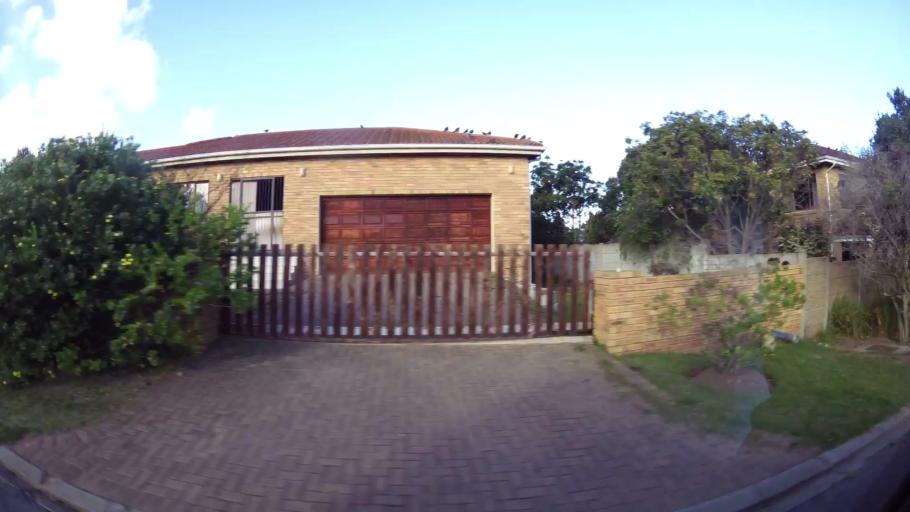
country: ZA
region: Western Cape
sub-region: Eden District Municipality
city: George
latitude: -33.9952
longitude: 22.6115
